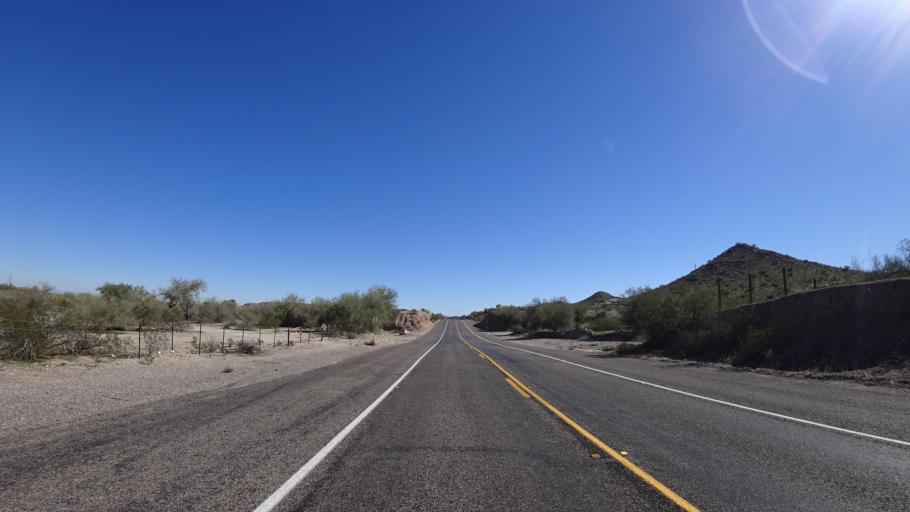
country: US
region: Arizona
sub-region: Maricopa County
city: Goodyear
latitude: 33.3754
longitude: -112.3622
